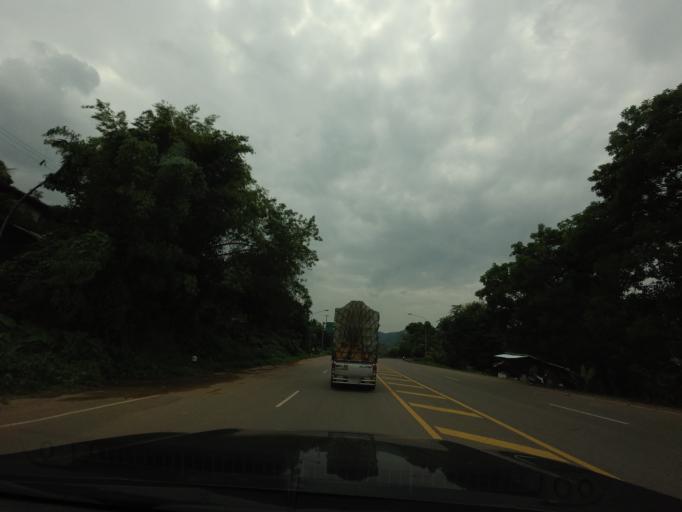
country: TH
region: Loei
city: Dan Sai
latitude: 17.2070
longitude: 101.1632
